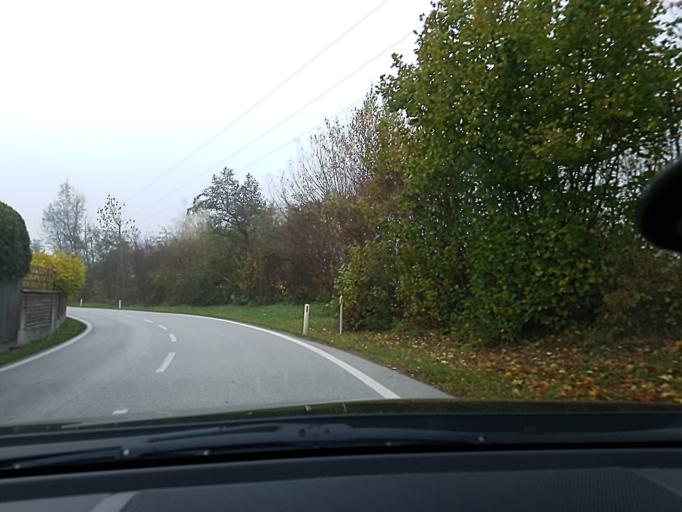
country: AT
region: Salzburg
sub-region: Politischer Bezirk Sankt Johann im Pongau
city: Sankt Johann im Pongau
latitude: 47.3696
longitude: 13.2108
